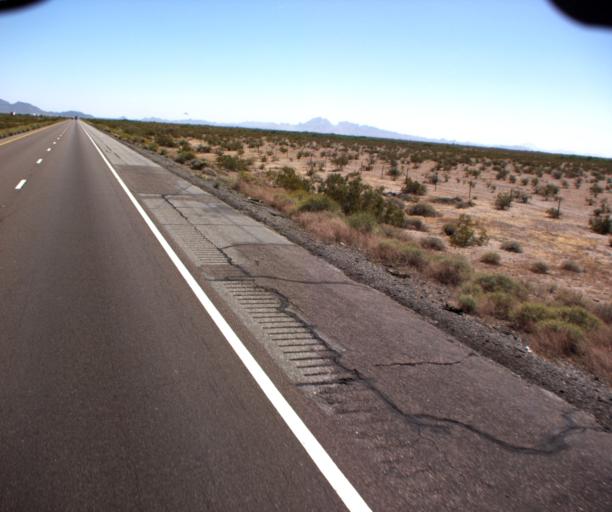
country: US
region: Arizona
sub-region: La Paz County
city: Salome
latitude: 33.5540
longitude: -113.2559
